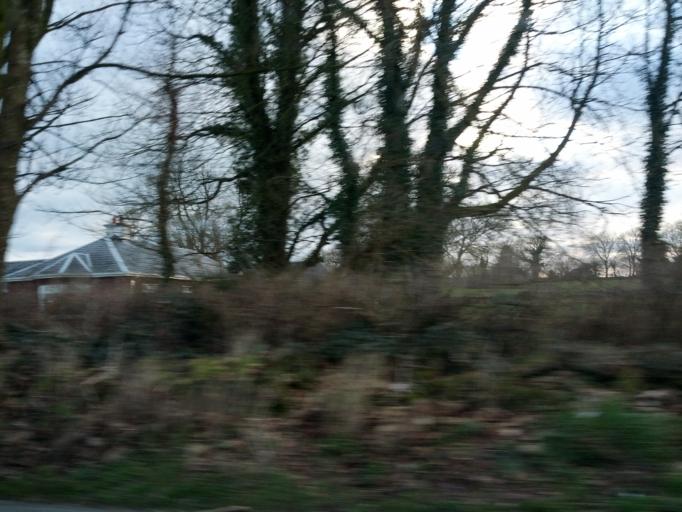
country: IE
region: Connaught
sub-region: County Galway
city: Athenry
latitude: 53.4382
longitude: -8.7215
